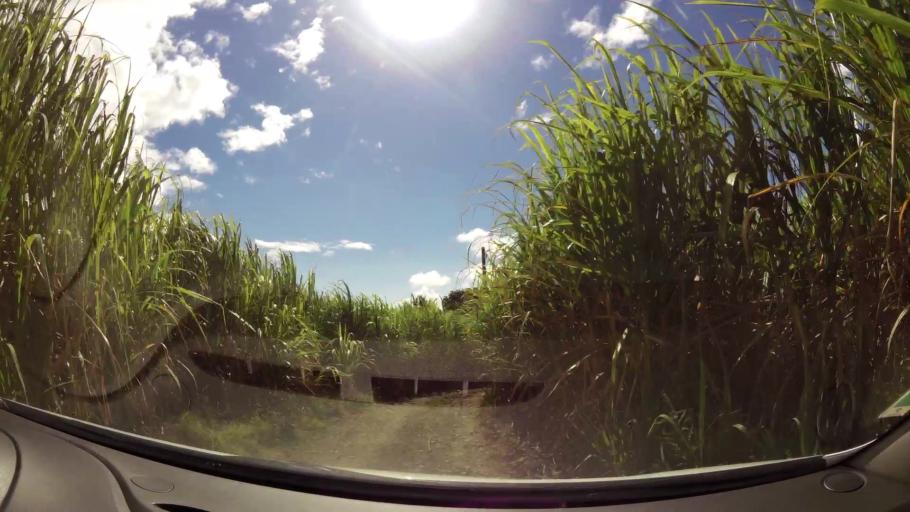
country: RE
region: Reunion
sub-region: Reunion
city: Sainte-Marie
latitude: -20.9254
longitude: 55.5055
